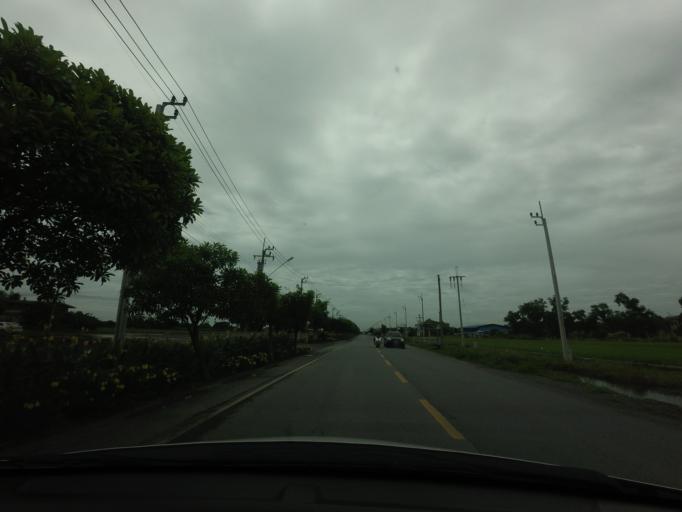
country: TH
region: Bangkok
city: Nong Chok
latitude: 13.8577
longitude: 100.8072
